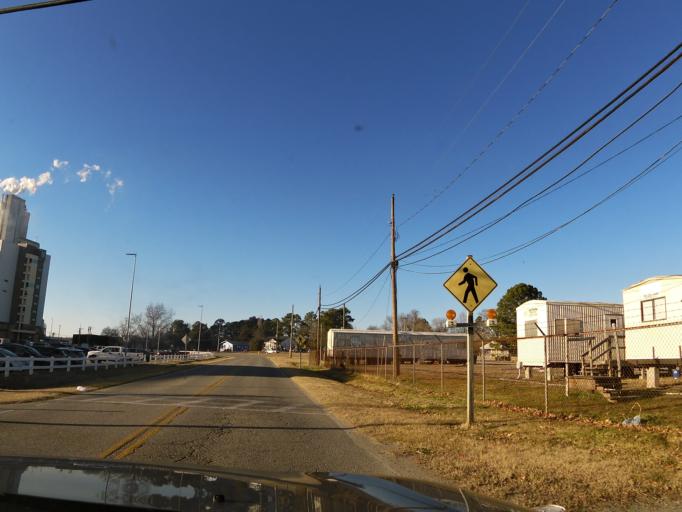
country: US
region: Virginia
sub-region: City of Franklin
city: Franklin
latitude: 36.6794
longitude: -76.9088
